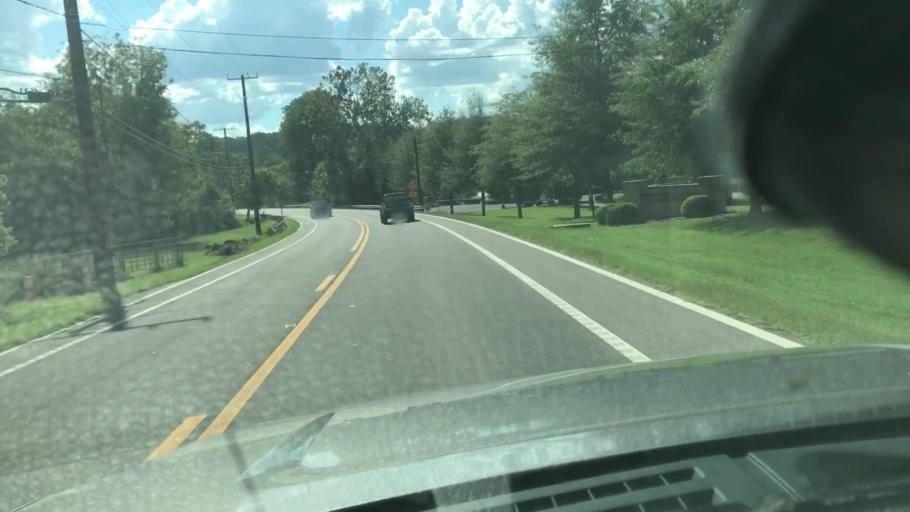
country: US
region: Tennessee
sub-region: Cheatham County
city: Pegram
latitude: 36.0268
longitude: -87.0196
